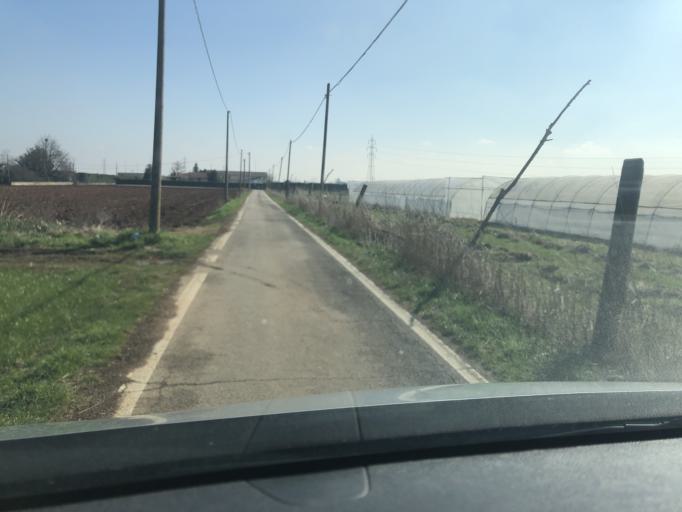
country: IT
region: Veneto
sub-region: Provincia di Verona
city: Villafranca di Verona
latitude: 45.3721
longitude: 10.8255
